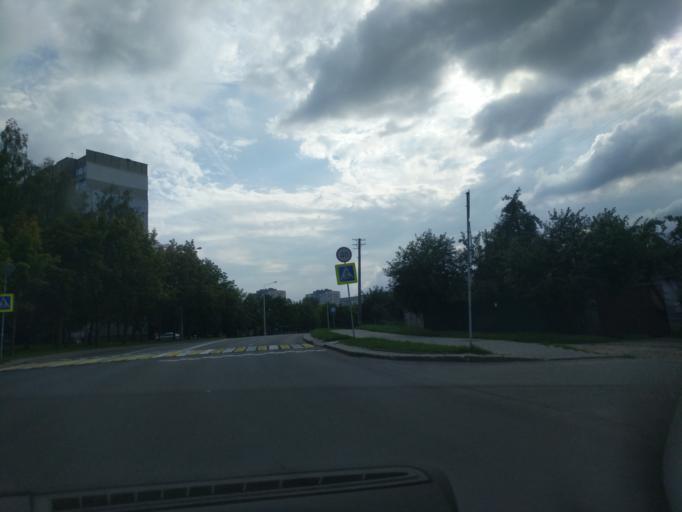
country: BY
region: Minsk
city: Malinovka
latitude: 53.8527
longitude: 27.4657
